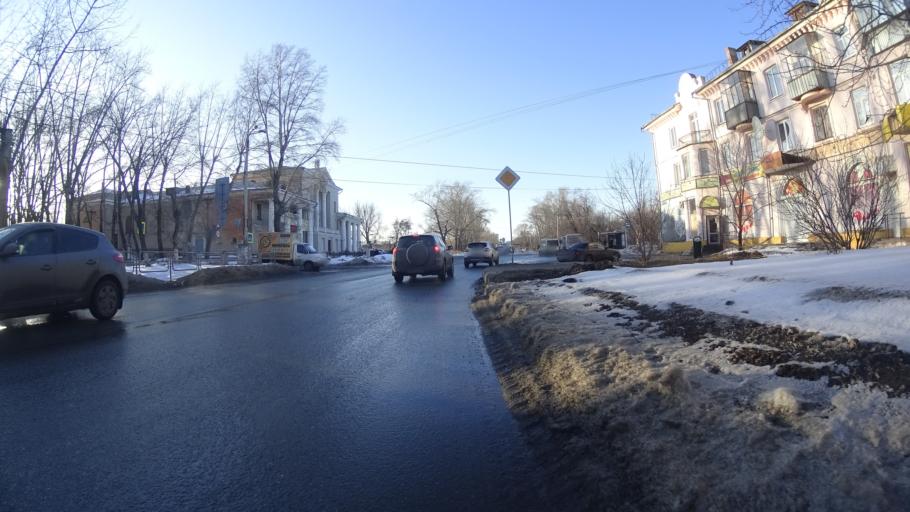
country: RU
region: Chelyabinsk
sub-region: Gorod Chelyabinsk
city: Chelyabinsk
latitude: 55.1301
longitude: 61.4650
